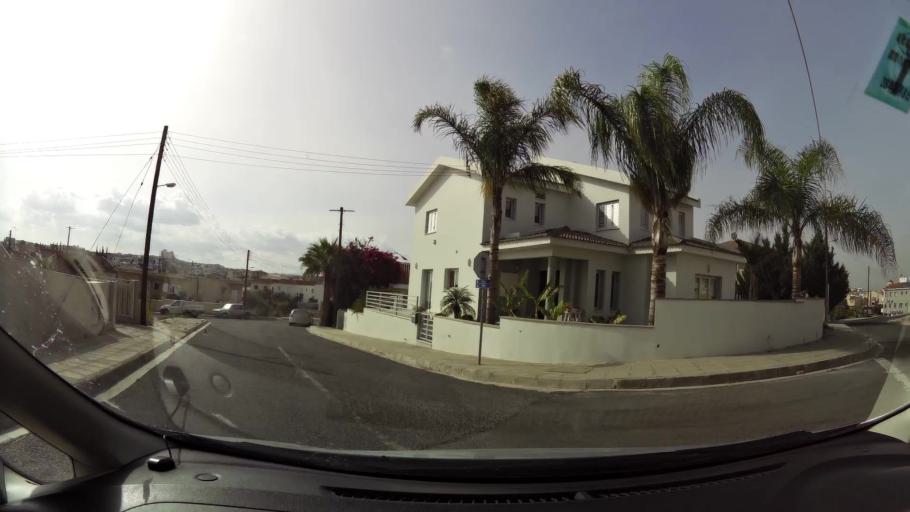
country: CY
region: Lefkosia
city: Geri
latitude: 35.0742
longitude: 33.3929
